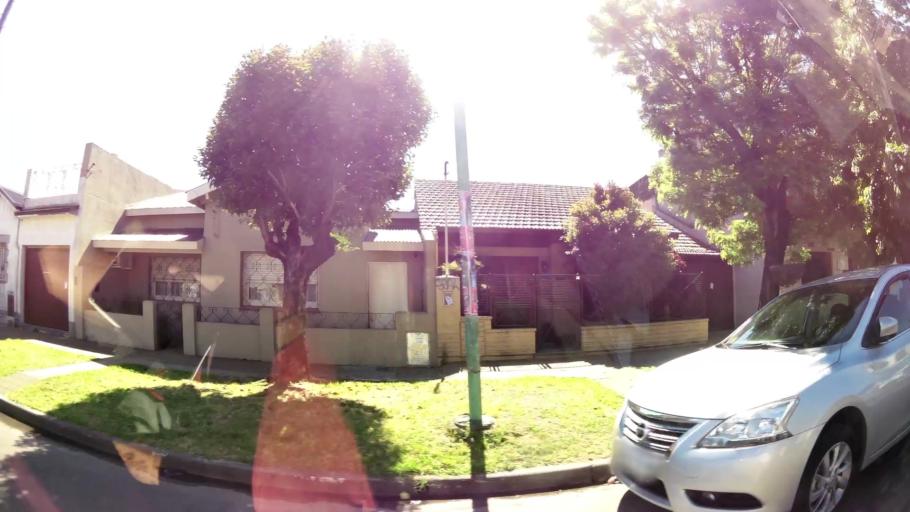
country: AR
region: Buenos Aires
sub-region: Partido de Lomas de Zamora
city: Lomas de Zamora
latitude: -34.7575
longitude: -58.4216
